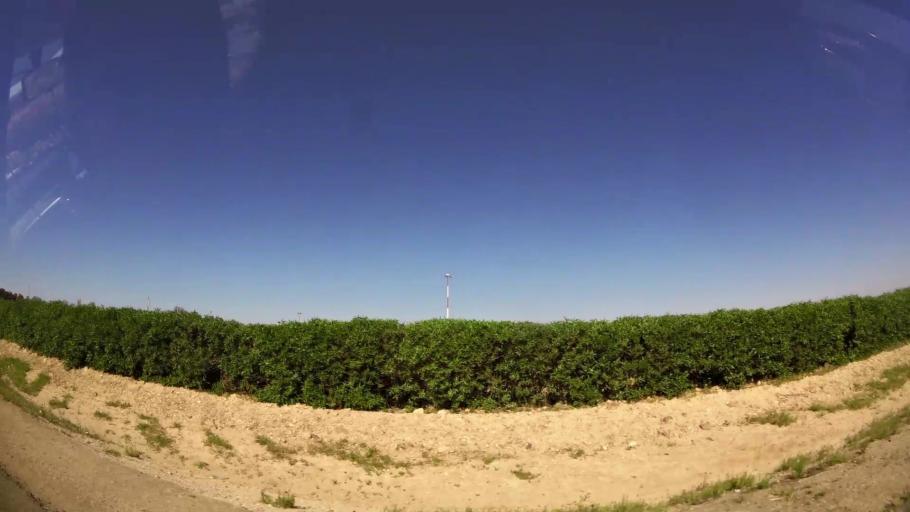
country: MA
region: Oriental
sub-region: Oujda-Angad
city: Oujda
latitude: 34.7822
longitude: -1.9474
